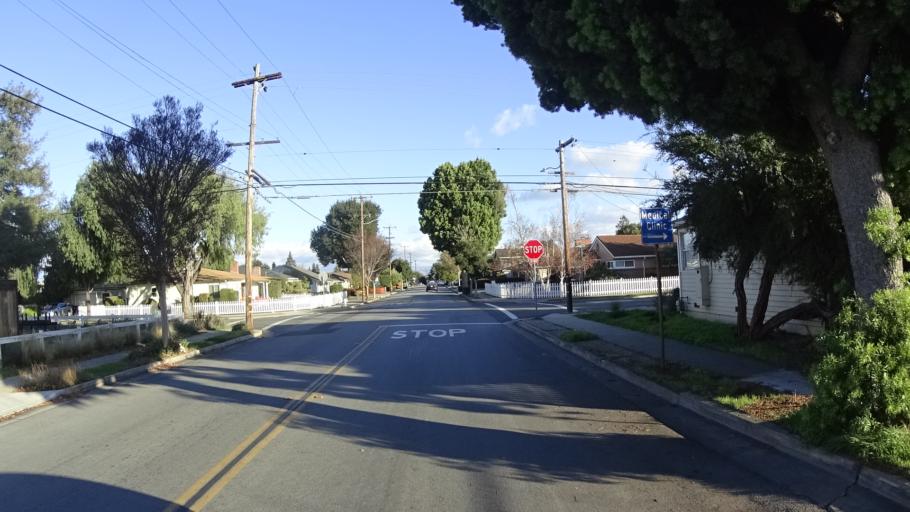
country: US
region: California
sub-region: Santa Clara County
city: Sunnyvale
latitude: 37.3708
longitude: -122.0303
